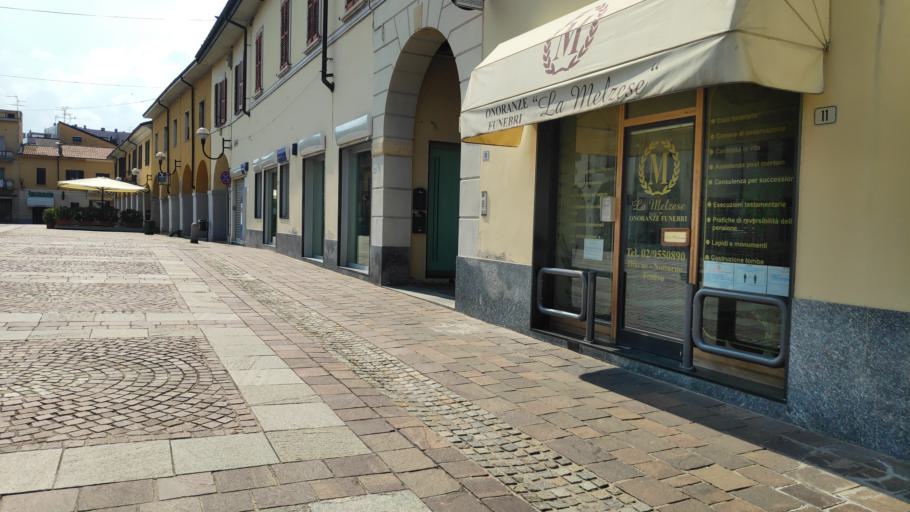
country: IT
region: Lombardy
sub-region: Citta metropolitana di Milano
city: Melzo
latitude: 45.4989
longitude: 9.4242
